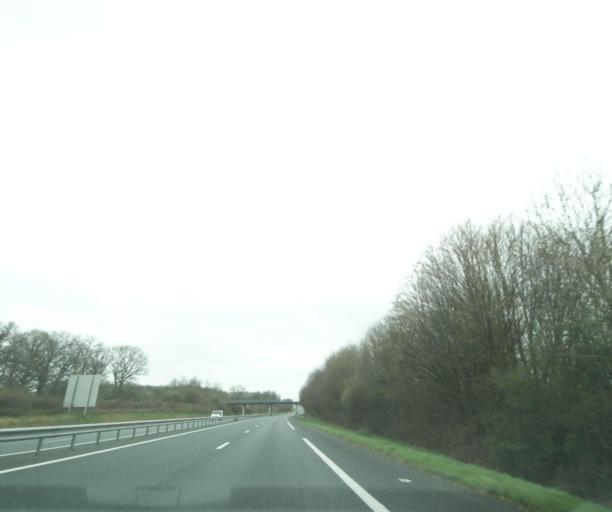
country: FR
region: Centre
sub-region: Departement de l'Indre
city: Chantome
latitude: 46.4308
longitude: 1.4766
